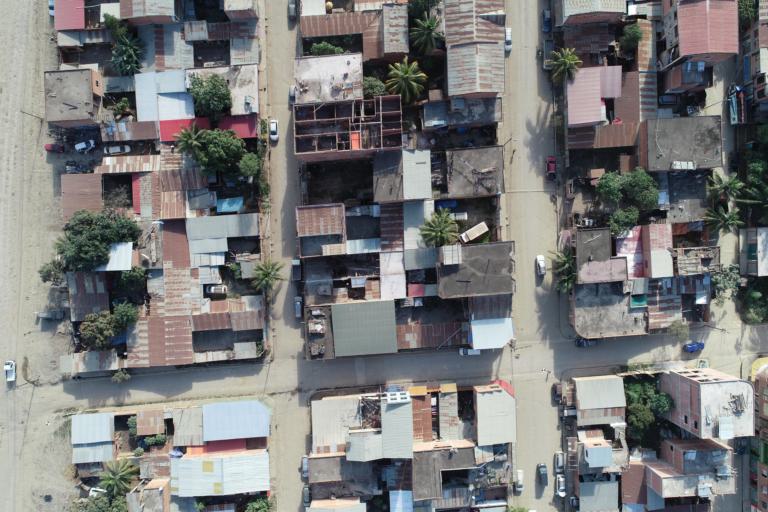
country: BO
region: La Paz
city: Coroico
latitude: -15.8364
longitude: -67.5616
